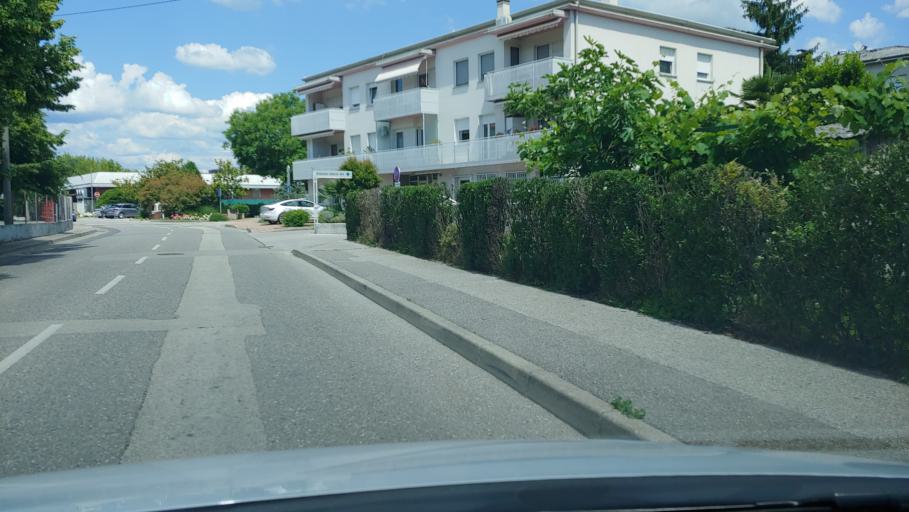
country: SI
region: Sempeter-Vrtojba
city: Sempeter pri Gorici
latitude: 45.9292
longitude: 13.6375
